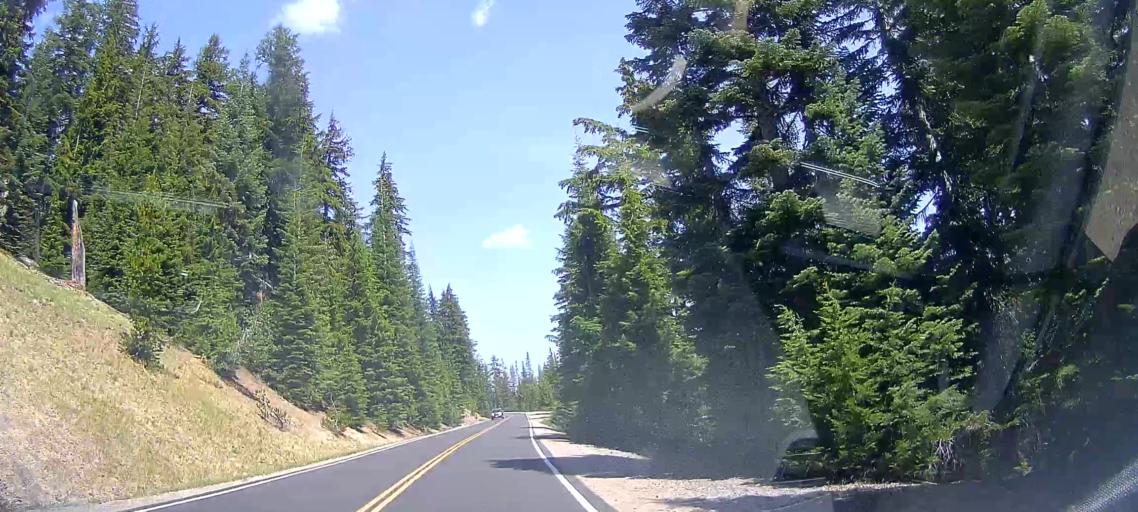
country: US
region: Oregon
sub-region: Jackson County
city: Shady Cove
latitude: 42.9784
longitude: -122.1069
